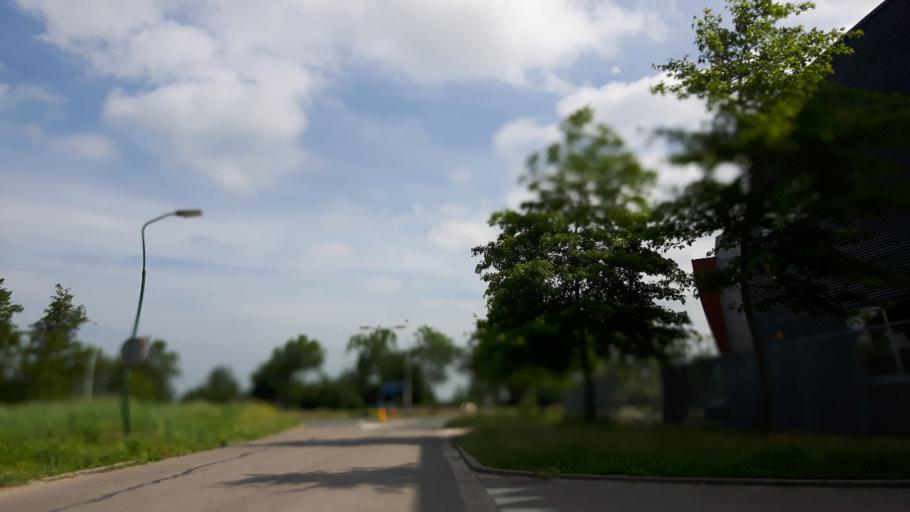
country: NL
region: Utrecht
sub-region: Gemeente De Ronde Venen
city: Mijdrecht
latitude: 52.1562
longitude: 4.8696
